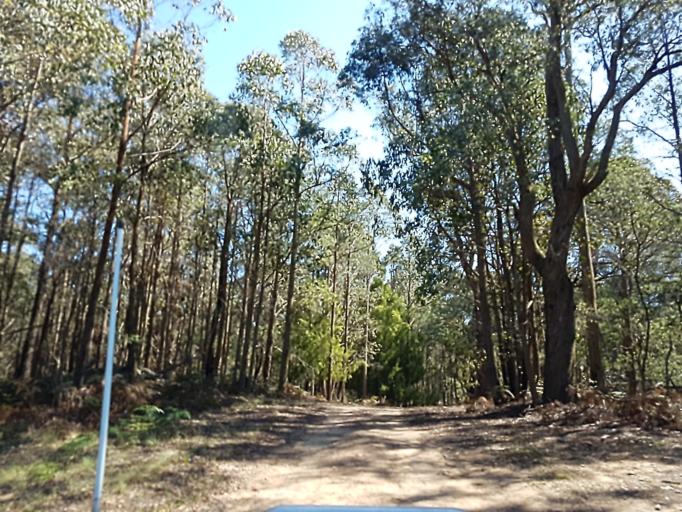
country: AU
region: Victoria
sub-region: East Gippsland
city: Lakes Entrance
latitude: -37.2340
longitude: 148.2877
